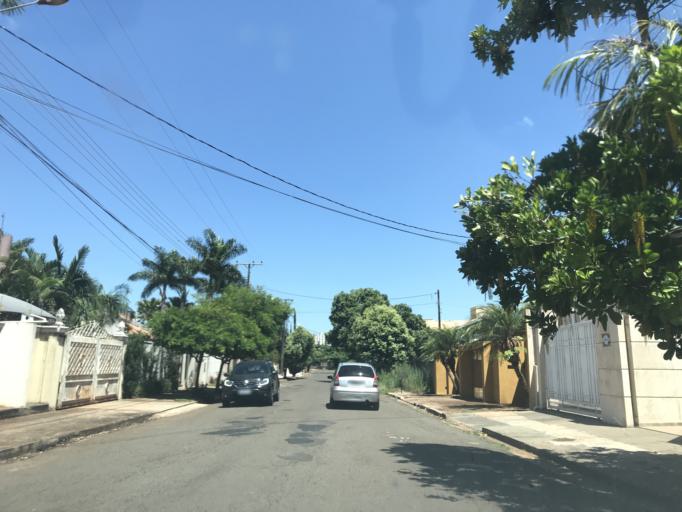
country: BR
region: Parana
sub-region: Londrina
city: Londrina
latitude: -23.3482
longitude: -51.1626
